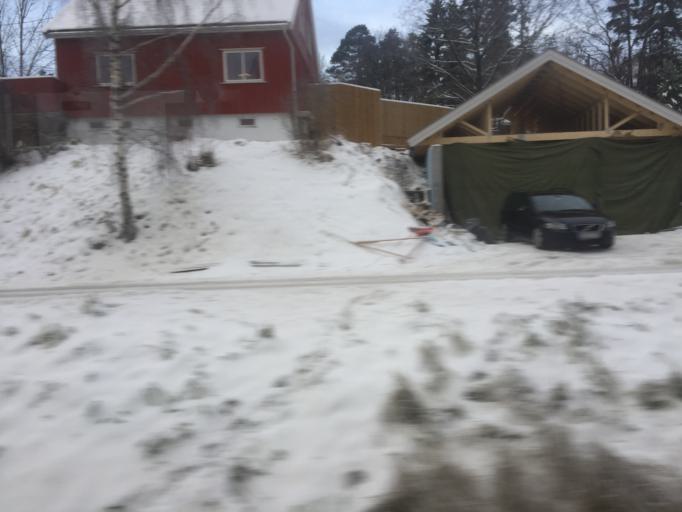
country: NO
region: Akershus
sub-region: Ski
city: Ski
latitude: 59.7372
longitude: 10.7621
